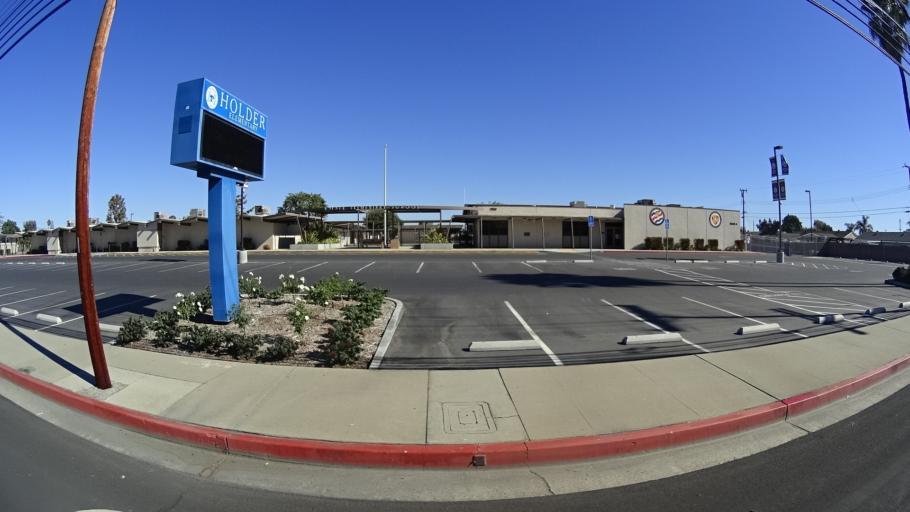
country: US
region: California
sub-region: Orange County
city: Cypress
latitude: 33.8230
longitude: -118.0196
